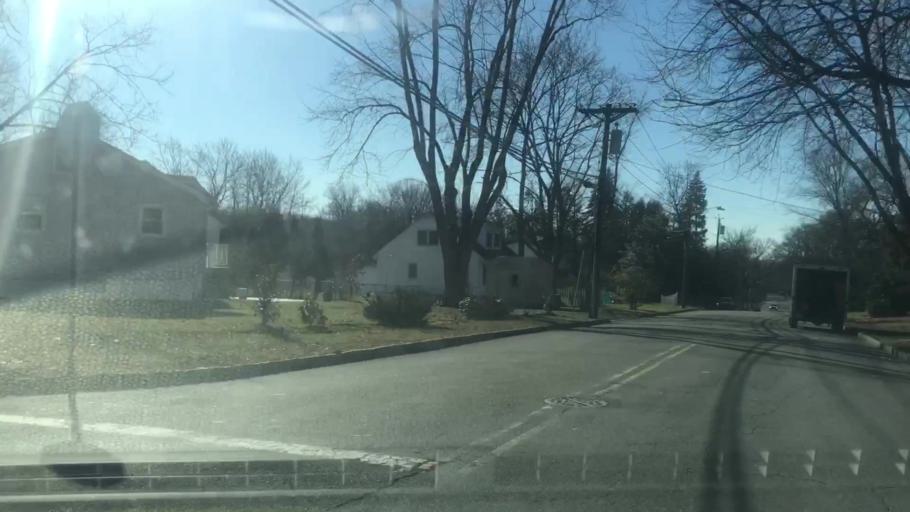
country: US
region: New Jersey
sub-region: Essex County
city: Livingston
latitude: 40.7800
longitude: -74.3002
